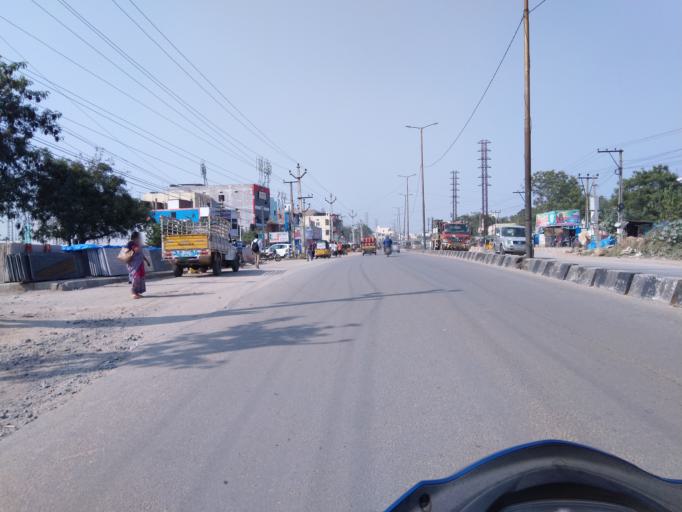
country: IN
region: Telangana
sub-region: Rangareddi
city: Quthbullapur
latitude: 17.5354
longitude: 78.4349
